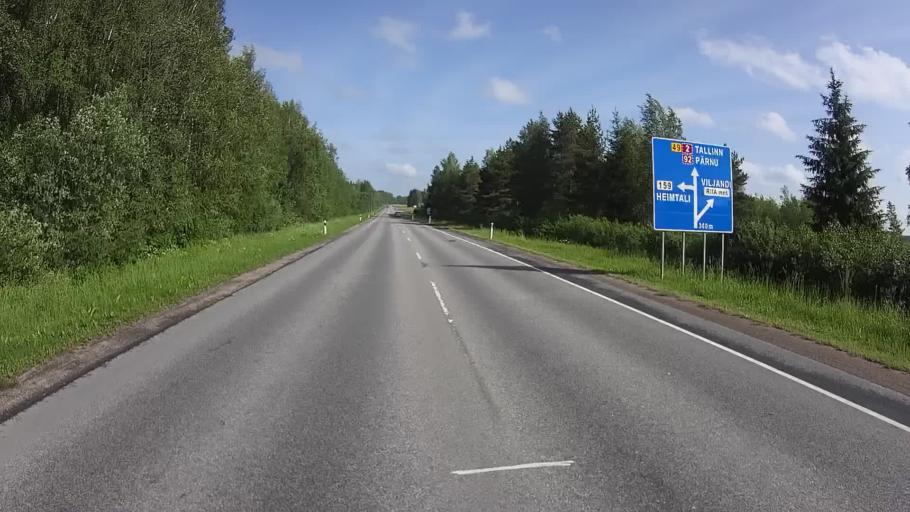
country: EE
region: Viljandimaa
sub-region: Viljandi linn
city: Viljandi
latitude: 58.3328
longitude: 25.5743
